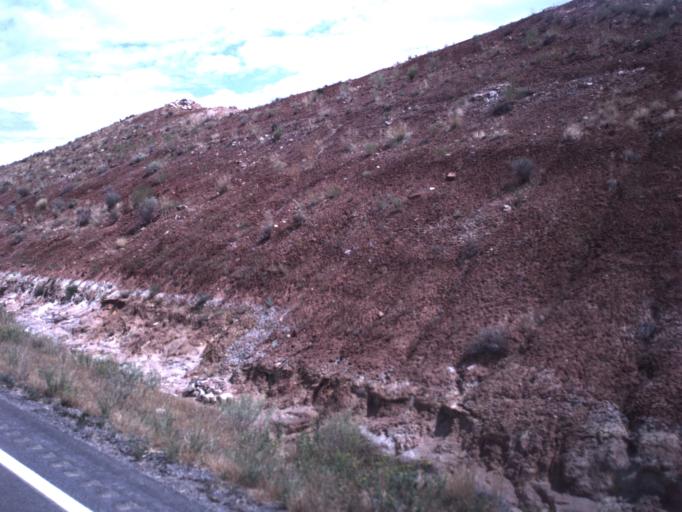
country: US
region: Utah
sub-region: Uintah County
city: Naples
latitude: 40.3200
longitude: -109.4857
